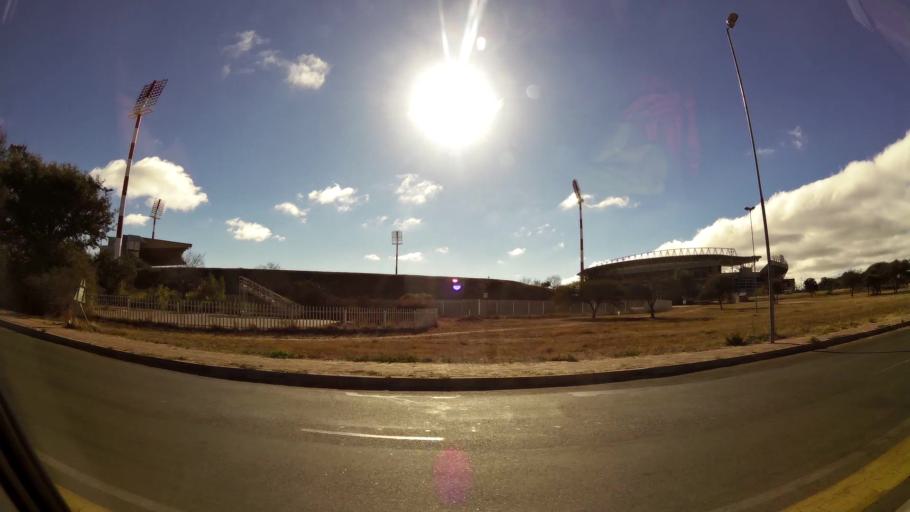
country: ZA
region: Limpopo
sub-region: Capricorn District Municipality
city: Polokwane
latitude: -23.9257
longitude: 29.4641
